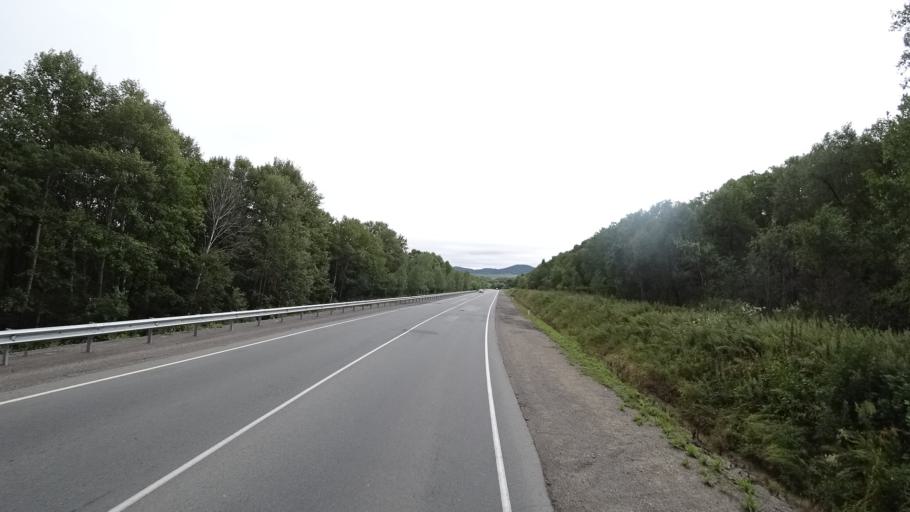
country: RU
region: Primorskiy
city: Lyalichi
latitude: 44.1039
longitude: 132.4234
